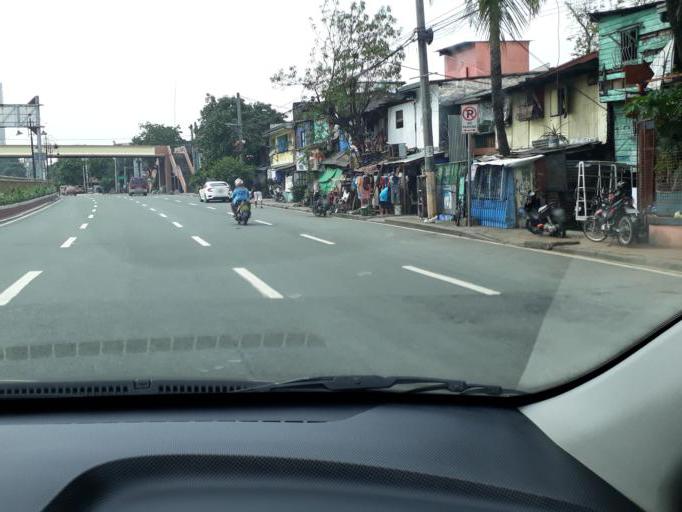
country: PH
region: Metro Manila
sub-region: City of Manila
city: Quiapo
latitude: 14.6040
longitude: 120.9979
